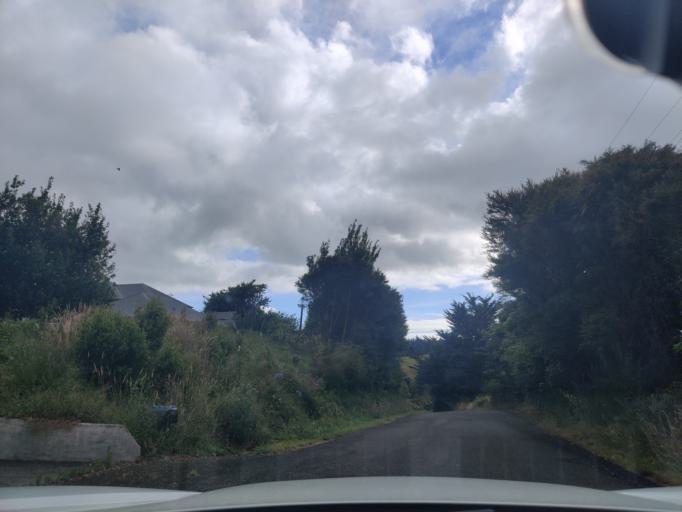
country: NZ
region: Manawatu-Wanganui
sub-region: Palmerston North City
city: Palmerston North
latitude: -40.3779
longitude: 175.6636
